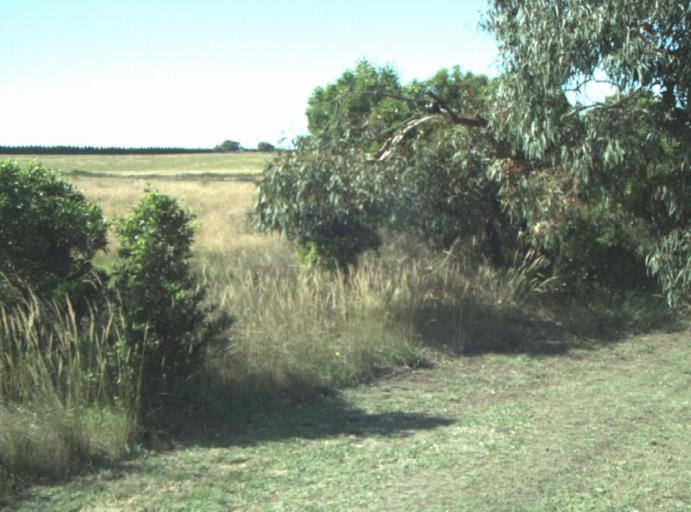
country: AU
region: Victoria
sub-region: Greater Geelong
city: Clifton Springs
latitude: -38.2257
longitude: 144.5862
